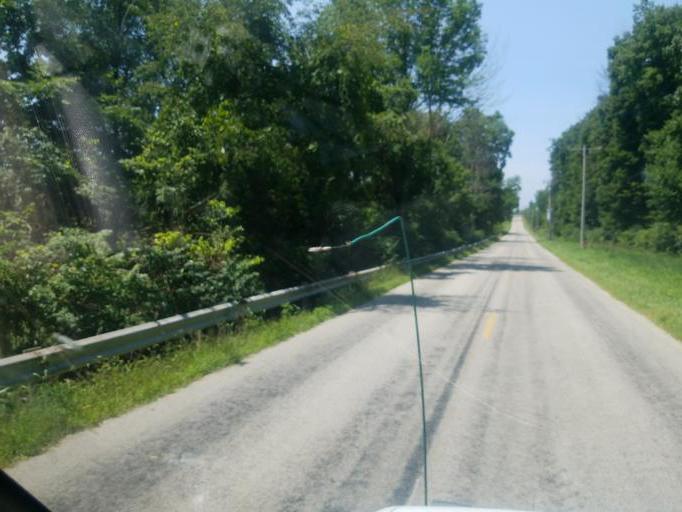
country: US
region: Ohio
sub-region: Shelby County
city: Sidney
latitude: 40.3057
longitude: -84.1020
